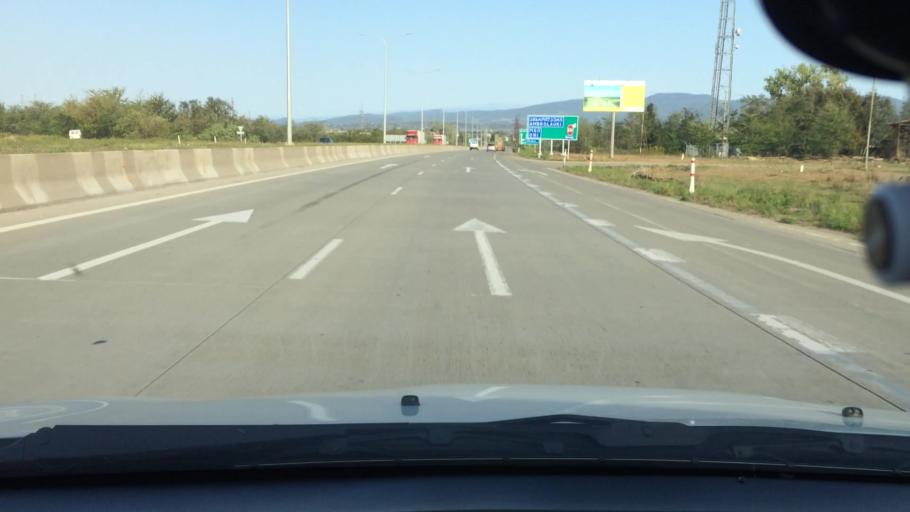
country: GE
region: Imereti
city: Zestap'oni
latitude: 42.1495
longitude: 42.9619
